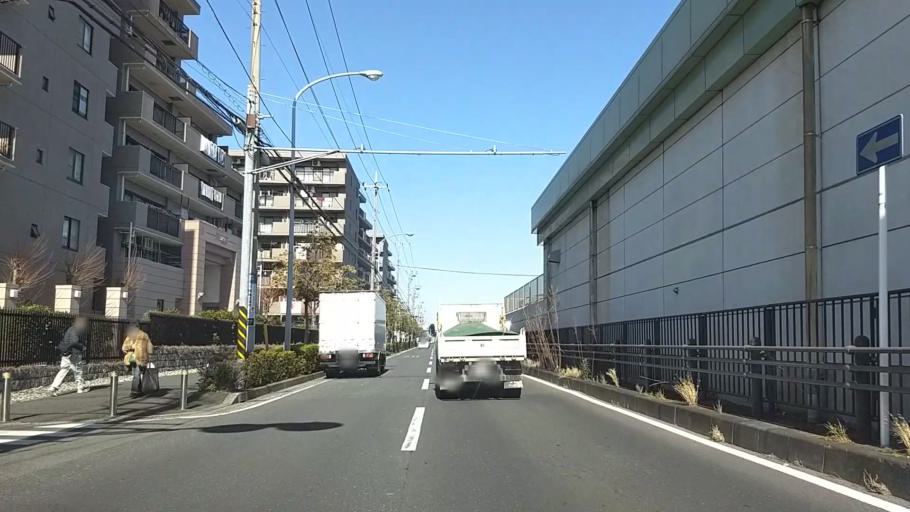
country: JP
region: Kanagawa
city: Yokohama
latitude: 35.5190
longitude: 139.6127
